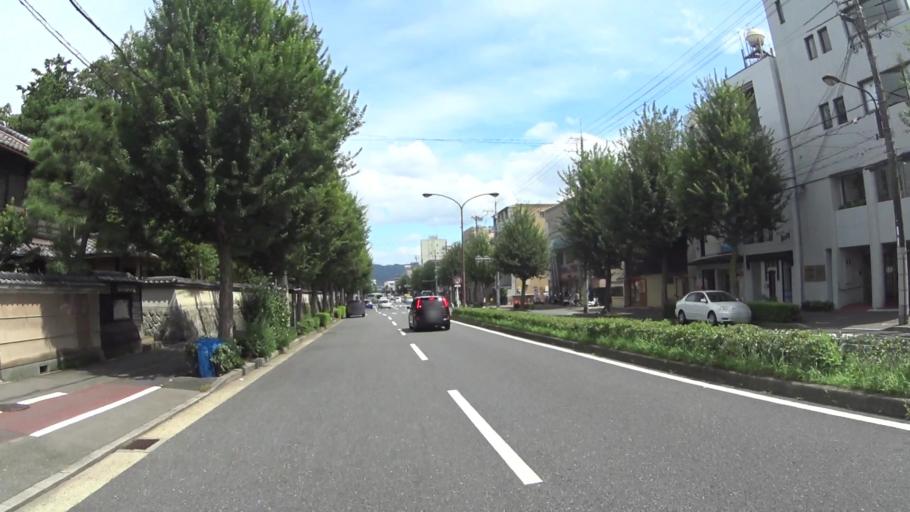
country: JP
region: Kyoto
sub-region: Kyoto-shi
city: Kamigyo-ku
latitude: 35.0408
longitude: 135.7456
